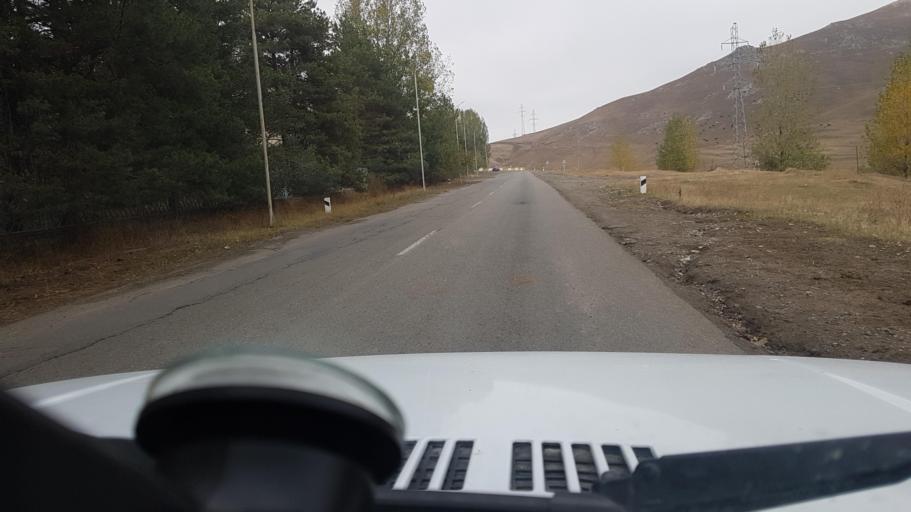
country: AZ
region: Gadabay Rayon
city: Ariqdam
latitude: 40.6101
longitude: 45.8127
